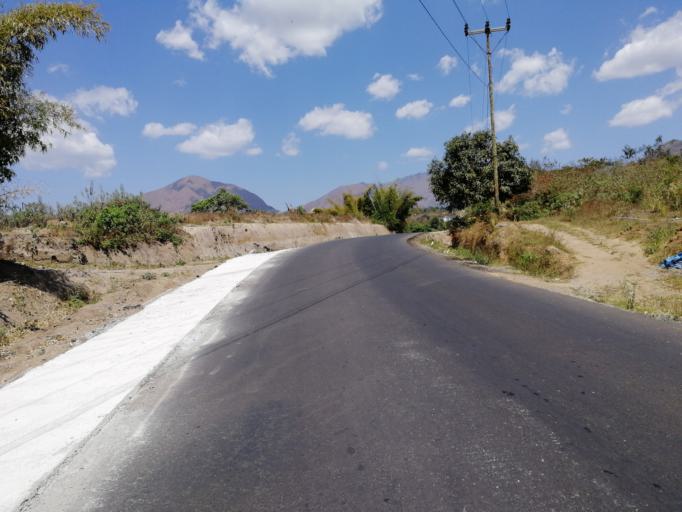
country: ID
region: West Nusa Tenggara
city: Sembalunlawang
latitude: -8.3520
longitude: 116.5105
